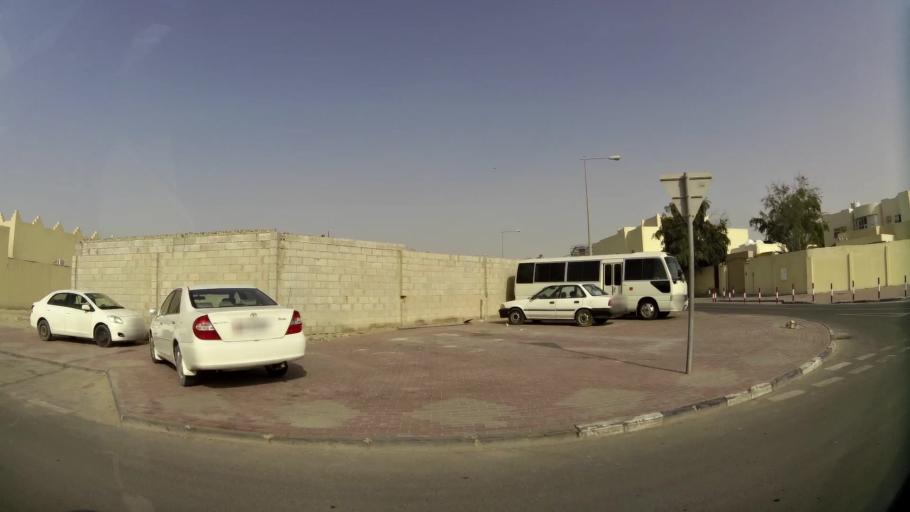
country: QA
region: Baladiyat ar Rayyan
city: Ar Rayyan
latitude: 25.2377
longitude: 51.4319
